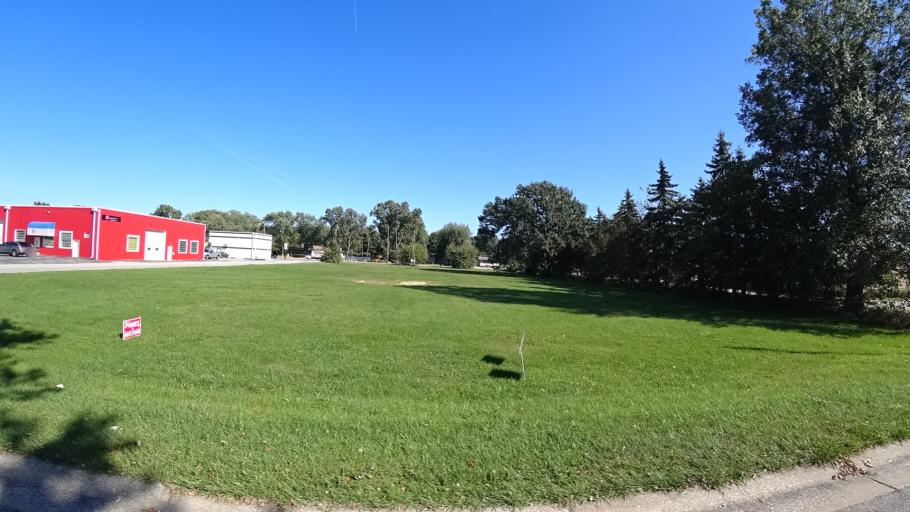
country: US
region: Indiana
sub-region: LaPorte County
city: Michigan City
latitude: 41.6896
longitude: -86.8953
